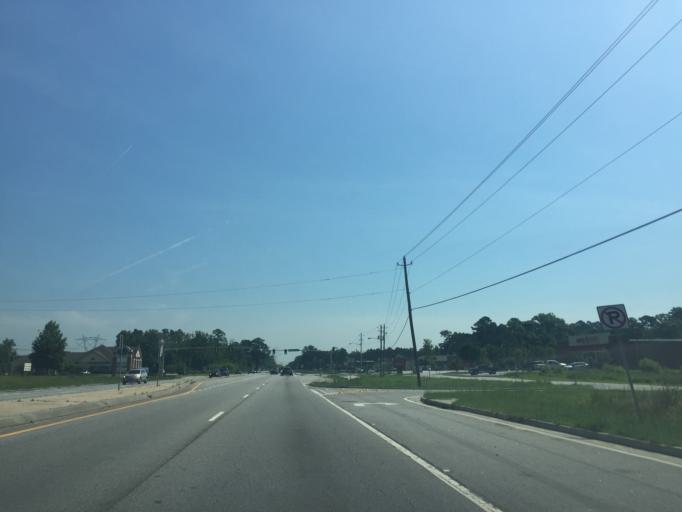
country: US
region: Georgia
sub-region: Bryan County
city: Richmond Hill
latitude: 31.9524
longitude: -81.3103
